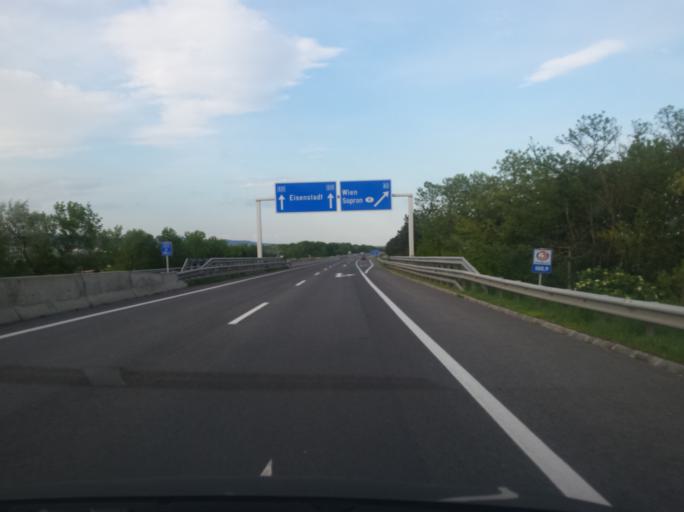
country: AT
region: Burgenland
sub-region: Eisenstadt-Umgebung
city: Wulkaprodersdorf
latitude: 47.8117
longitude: 16.4875
